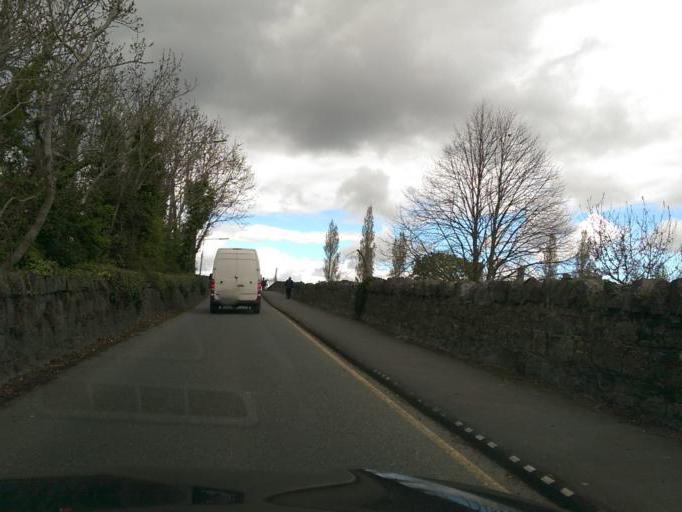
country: IE
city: Confey
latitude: 53.3735
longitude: -6.4853
